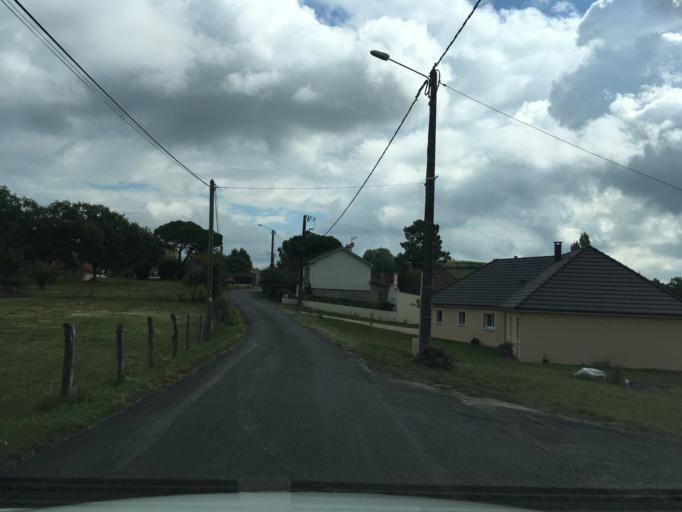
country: FR
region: Limousin
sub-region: Departement de la Correze
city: Brive-la-Gaillarde
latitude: 45.1112
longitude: 1.5371
